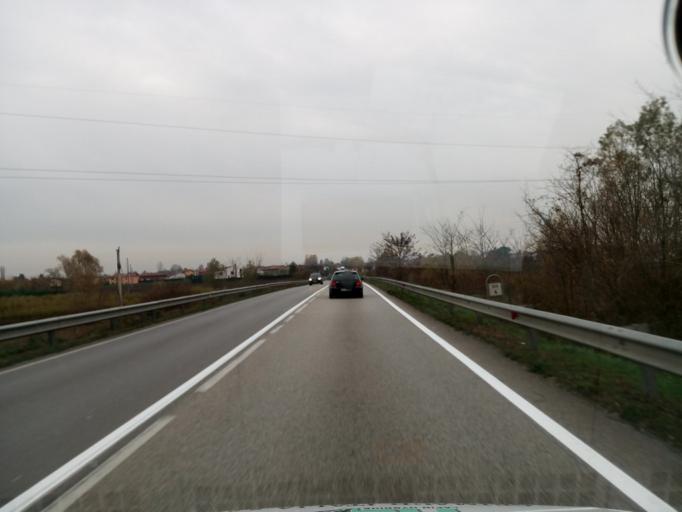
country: IT
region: Veneto
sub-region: Provincia di Padova
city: Saonara
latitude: 45.3618
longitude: 12.0012
